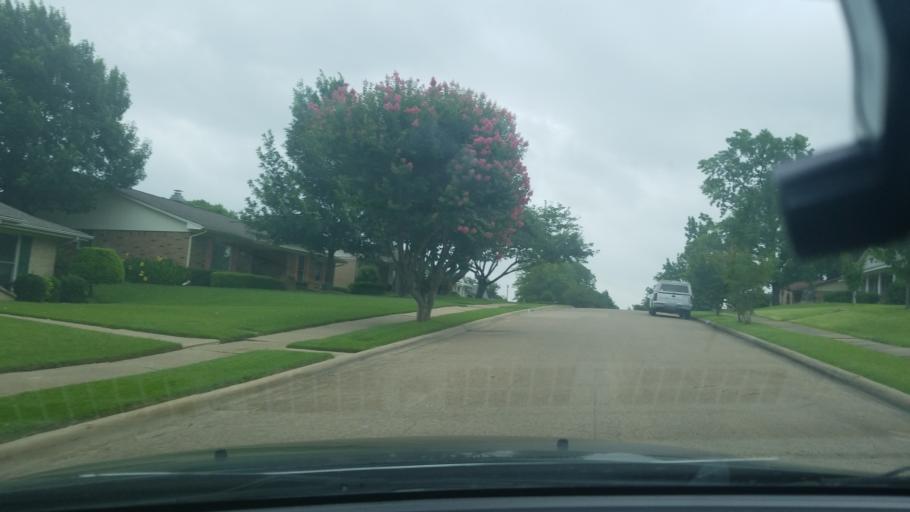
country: US
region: Texas
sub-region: Dallas County
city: Mesquite
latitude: 32.7817
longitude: -96.6341
